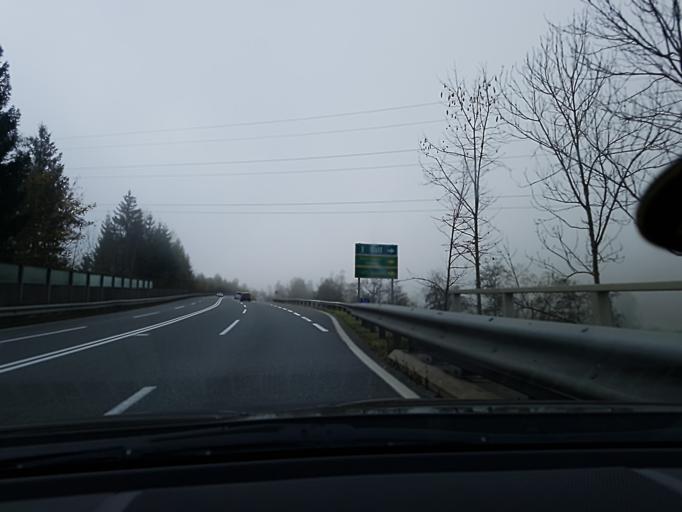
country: AT
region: Salzburg
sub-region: Politischer Bezirk Sankt Johann im Pongau
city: Bischofshofen
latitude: 47.3914
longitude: 13.2189
